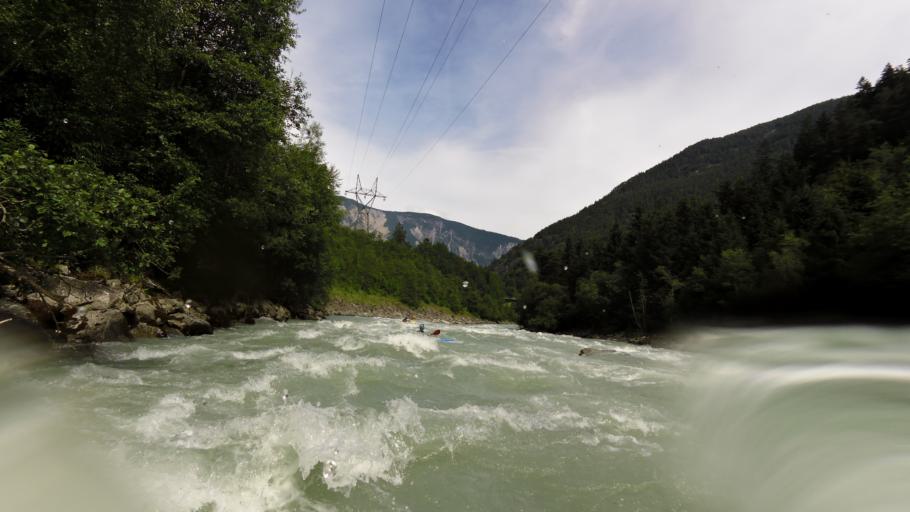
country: AT
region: Tyrol
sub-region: Politischer Bezirk Imst
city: Sautens
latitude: 47.2085
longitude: 10.8719
